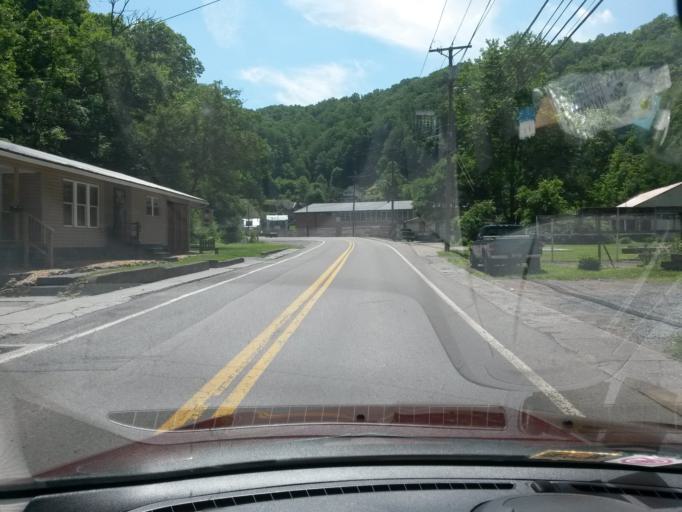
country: US
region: West Virginia
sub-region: McDowell County
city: Welch
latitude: 37.4407
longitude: -81.5779
